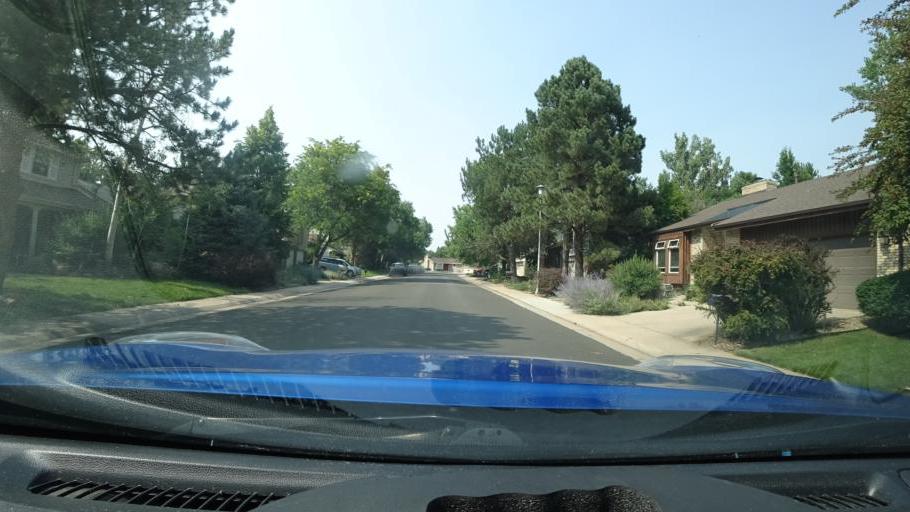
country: US
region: Colorado
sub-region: Adams County
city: Aurora
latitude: 39.6655
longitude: -104.8500
